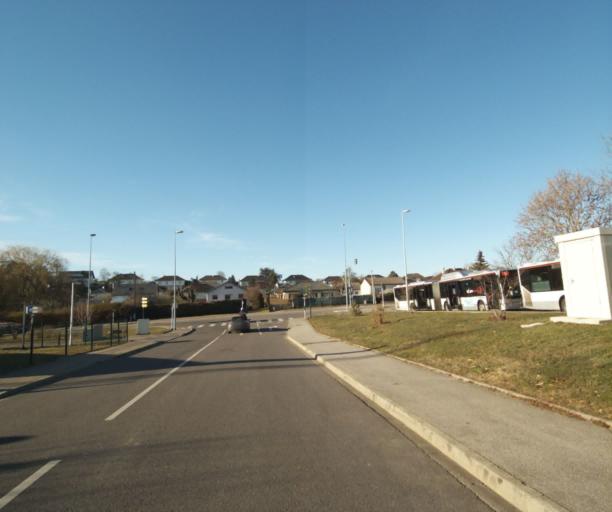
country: FR
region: Lorraine
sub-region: Departement de Meurthe-et-Moselle
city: Seichamps
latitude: 48.7192
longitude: 6.2658
